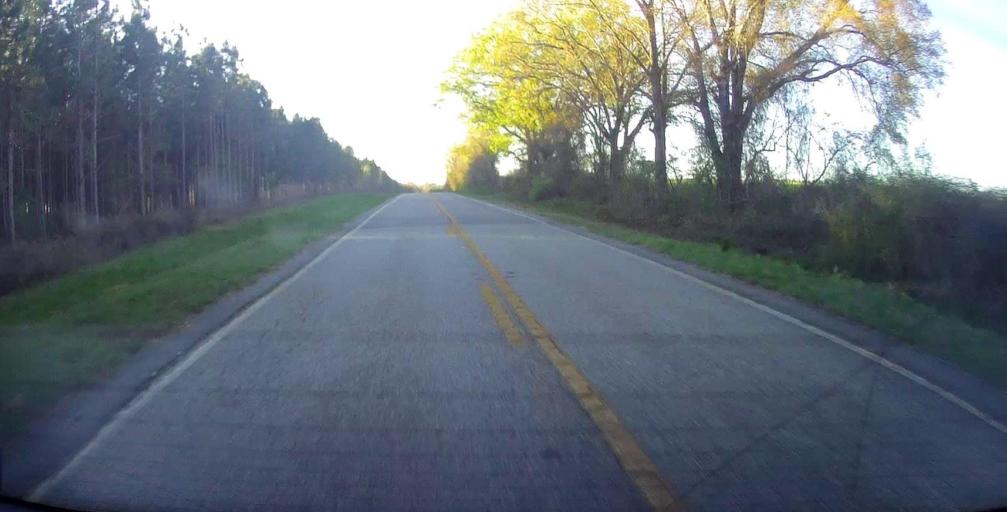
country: US
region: Georgia
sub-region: Wilcox County
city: Abbeville
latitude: 32.1125
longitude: -83.3193
